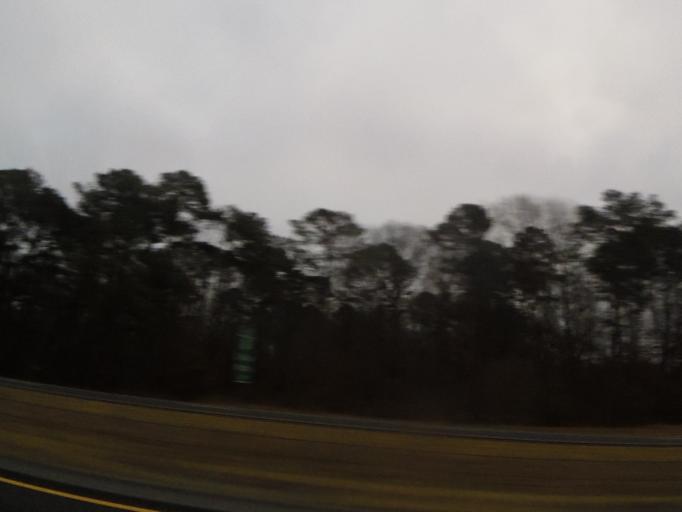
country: US
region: Alabama
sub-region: Cullman County
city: Cullman
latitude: 34.1967
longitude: -86.8784
